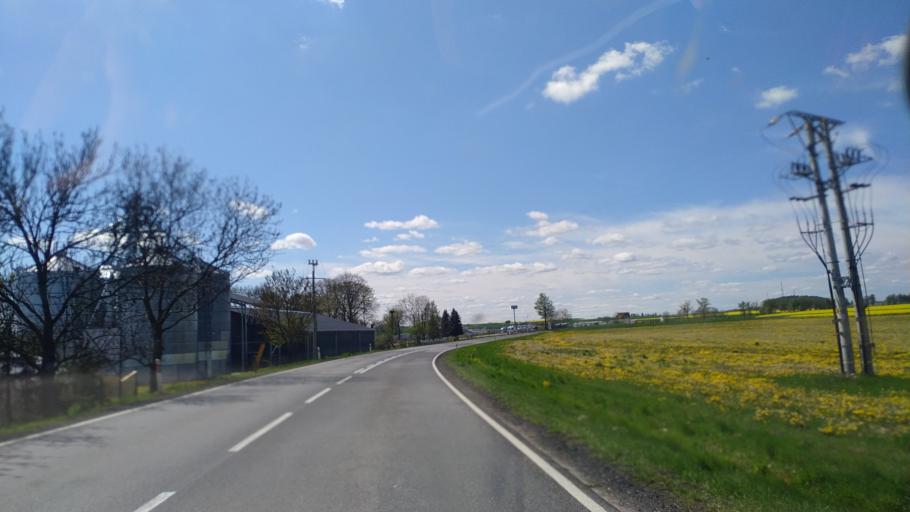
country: PL
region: Greater Poland Voivodeship
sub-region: Powiat pilski
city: Szydlowo
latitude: 53.2321
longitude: 16.6775
